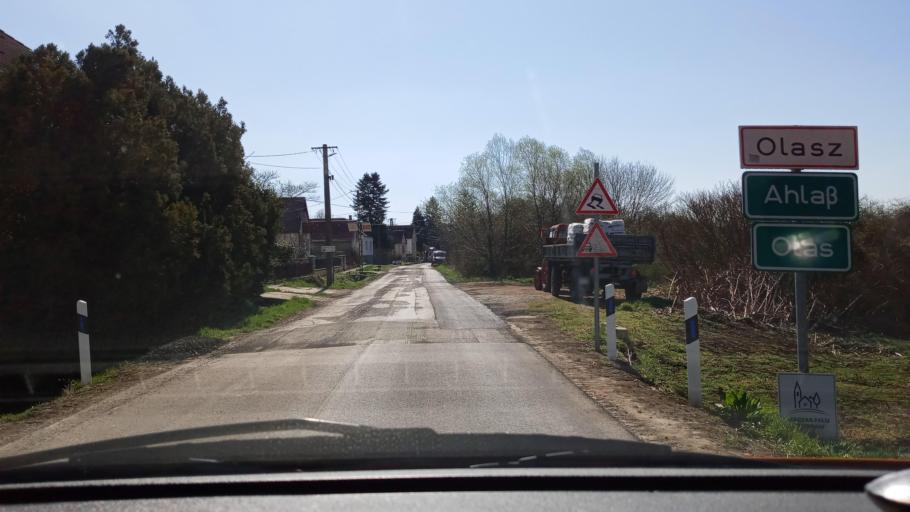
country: HU
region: Baranya
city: Kozarmisleny
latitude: 46.0209
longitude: 18.4060
